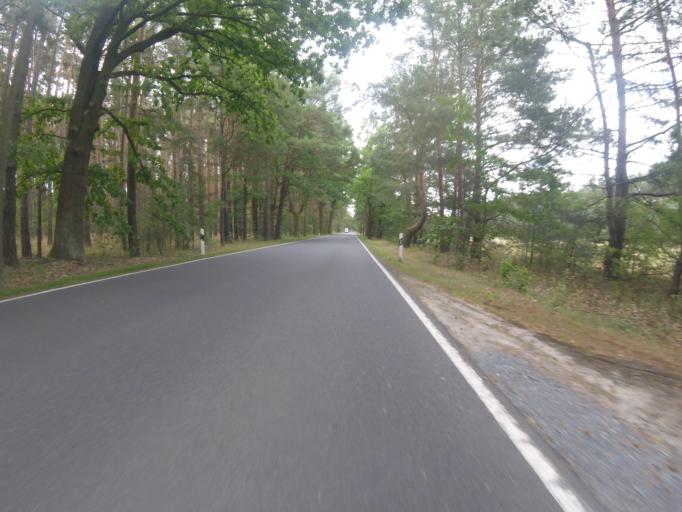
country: DE
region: Brandenburg
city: Bestensee
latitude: 52.2770
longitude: 13.7337
